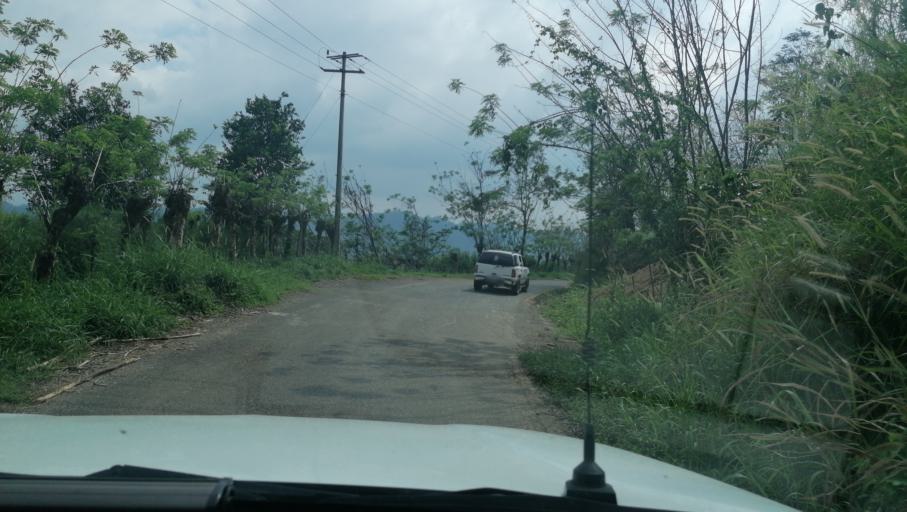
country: MX
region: Chiapas
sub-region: Francisco Leon
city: San Miguel la Sardina
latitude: 17.2338
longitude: -93.3323
